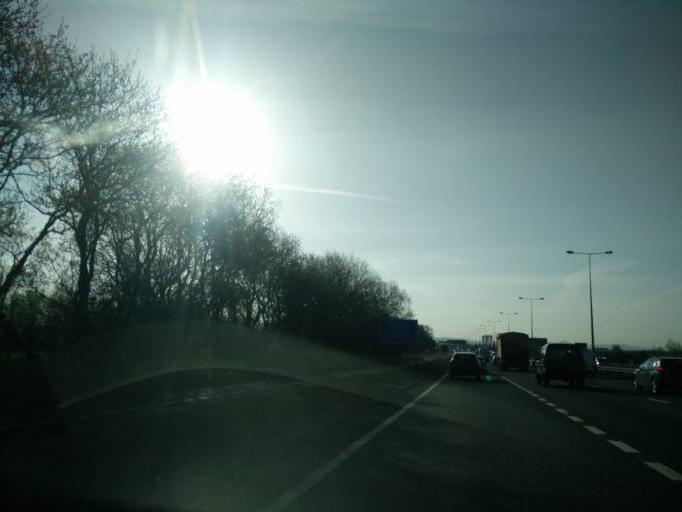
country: GB
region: England
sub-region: Stockton-on-Tees
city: Billingham
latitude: 54.5810
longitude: -1.2907
